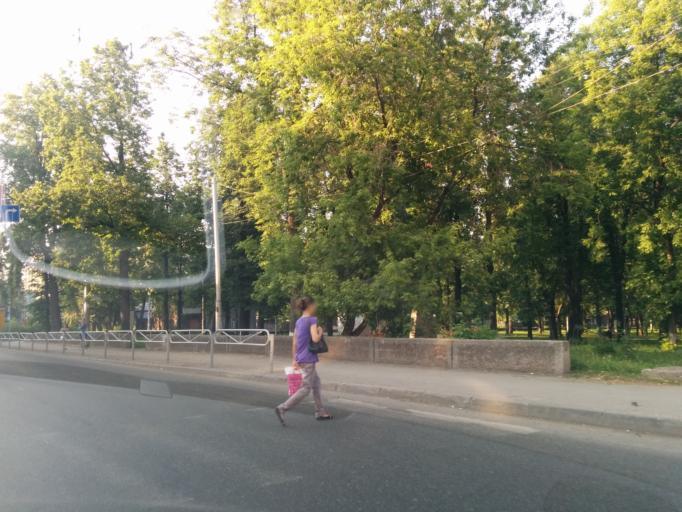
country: RU
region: Perm
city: Perm
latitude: 58.0127
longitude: 56.2592
